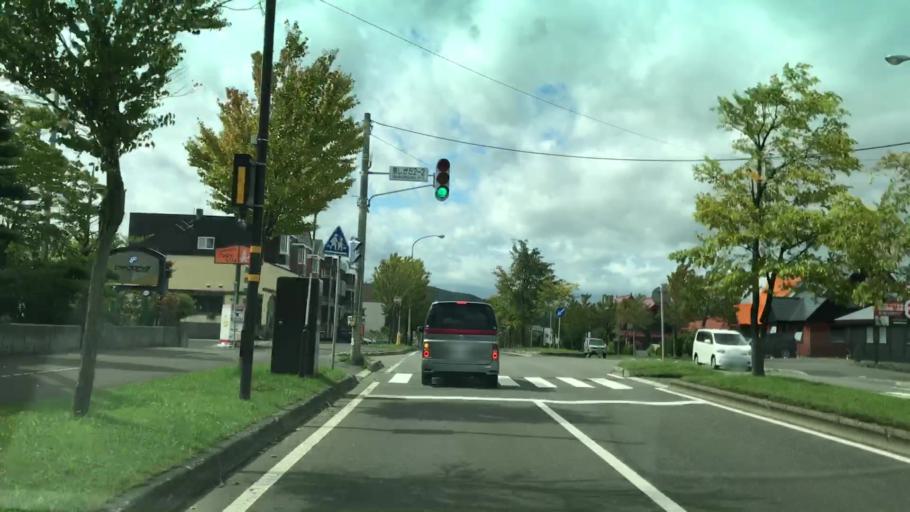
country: JP
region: Hokkaido
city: Kitahiroshima
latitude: 42.9885
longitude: 141.4489
